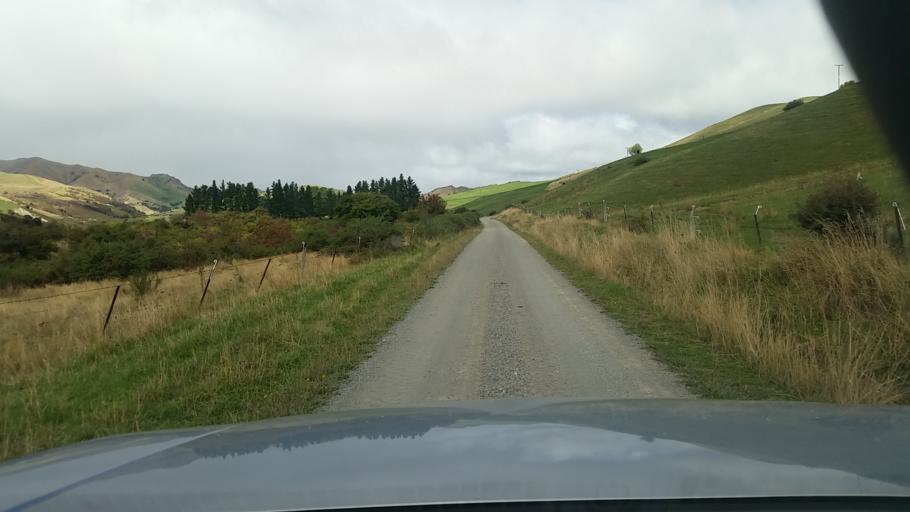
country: NZ
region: Marlborough
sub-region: Marlborough District
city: Blenheim
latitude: -41.7396
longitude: 173.8931
